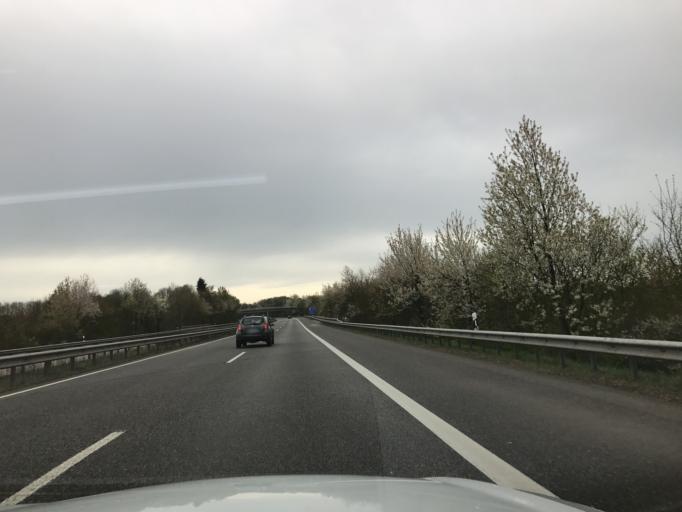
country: DE
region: Rheinland-Pfalz
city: Hasborn
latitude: 50.0557
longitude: 6.9030
